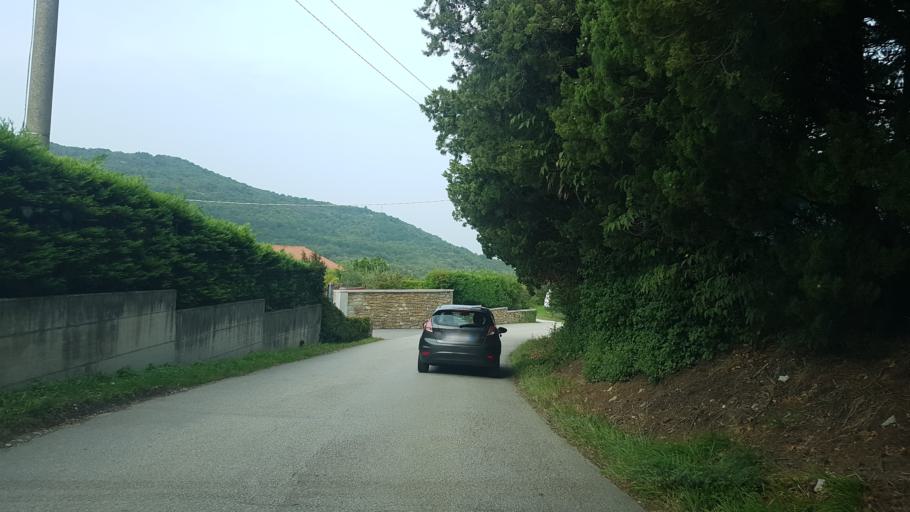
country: SI
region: Koper-Capodistria
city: Spodnje Skofije
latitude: 45.5833
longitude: 13.8017
